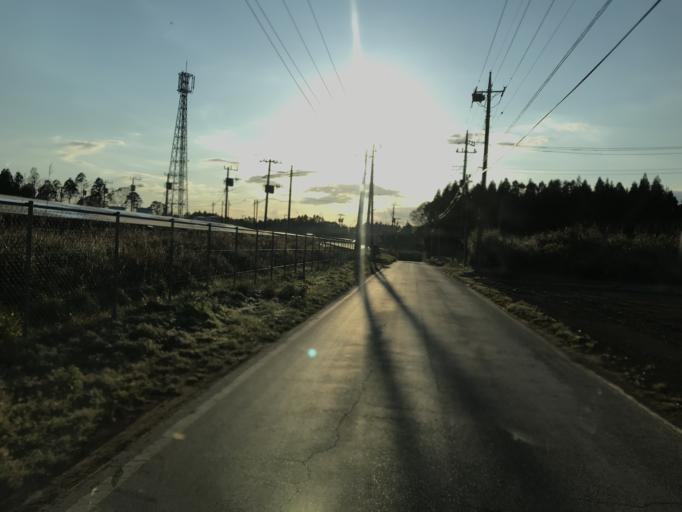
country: JP
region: Chiba
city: Yokaichiba
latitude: 35.7694
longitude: 140.5417
